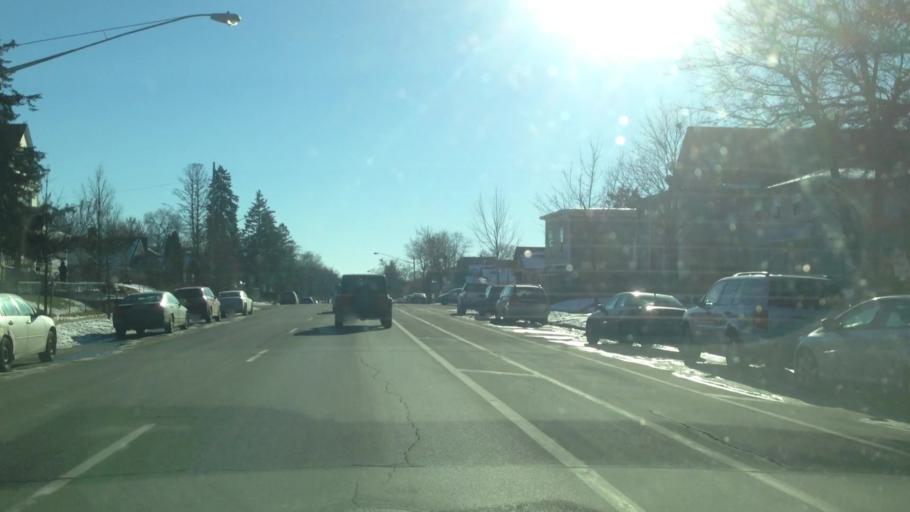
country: US
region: Minnesota
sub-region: Hennepin County
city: Minneapolis
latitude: 44.9331
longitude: -93.2676
